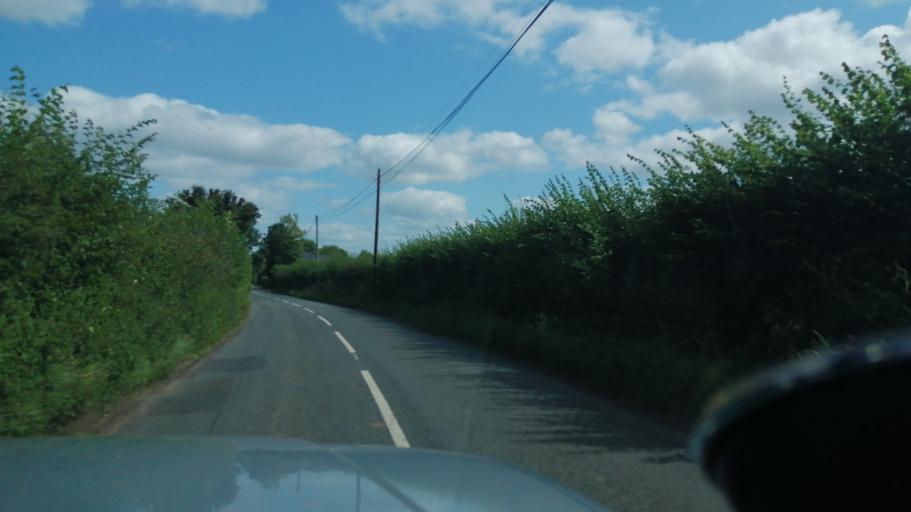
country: GB
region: England
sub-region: Herefordshire
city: Moccas
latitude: 52.0777
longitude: -2.9466
